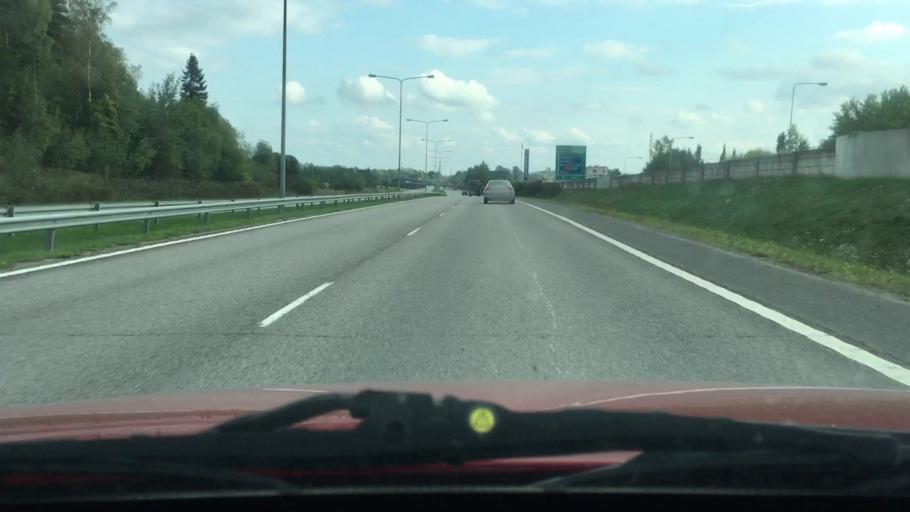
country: FI
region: Varsinais-Suomi
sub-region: Turku
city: Raisio
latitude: 60.4944
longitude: 22.1668
